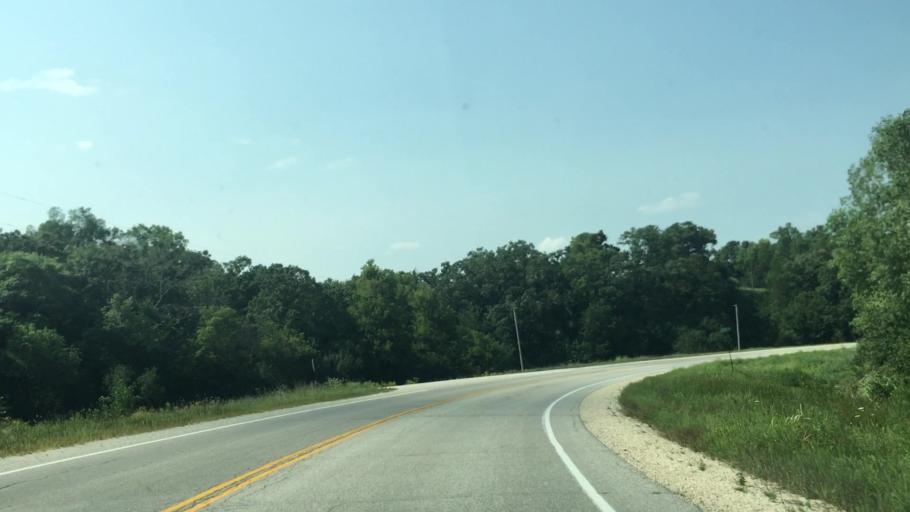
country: US
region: Minnesota
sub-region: Fillmore County
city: Preston
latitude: 43.7017
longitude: -91.9696
